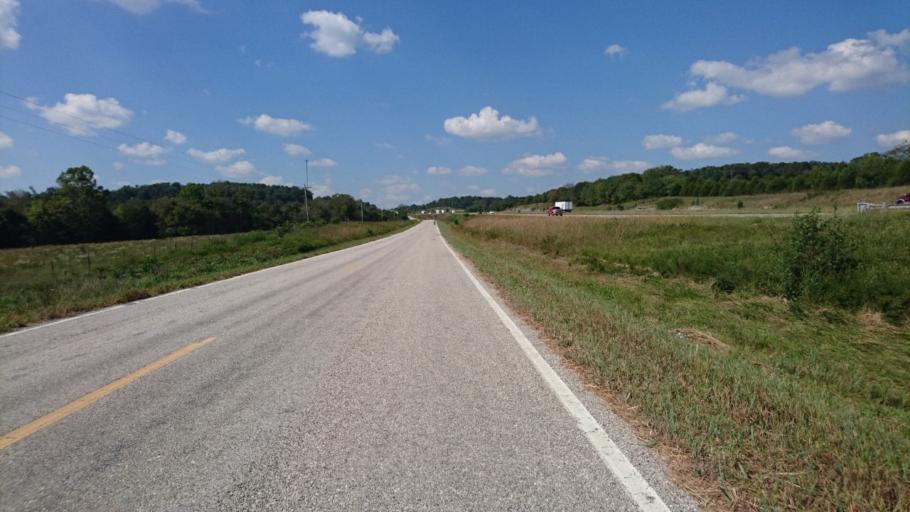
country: US
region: Missouri
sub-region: Pulaski County
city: Richland
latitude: 37.7575
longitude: -92.4675
